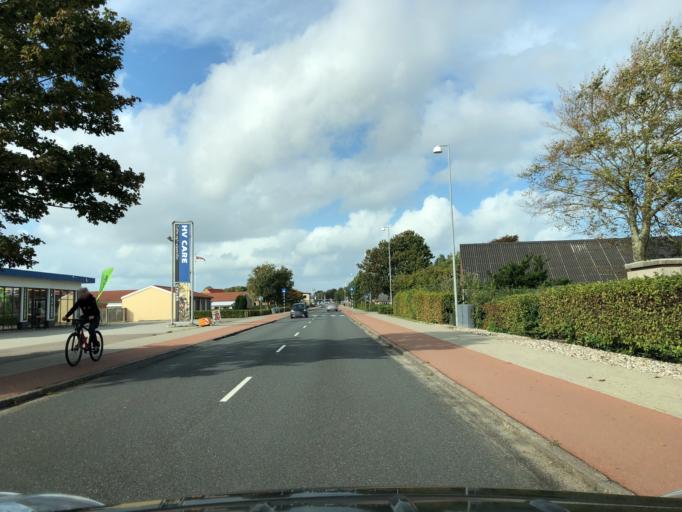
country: DK
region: Central Jutland
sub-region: Holstebro Kommune
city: Holstebro
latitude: 56.3723
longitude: 8.6163
